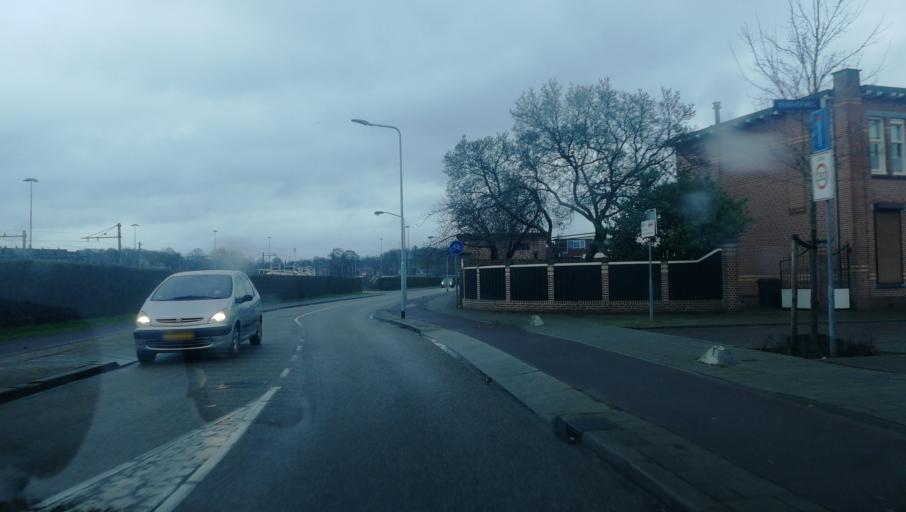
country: NL
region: Limburg
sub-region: Gemeente Venlo
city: Venlo
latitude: 51.3610
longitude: 6.1736
